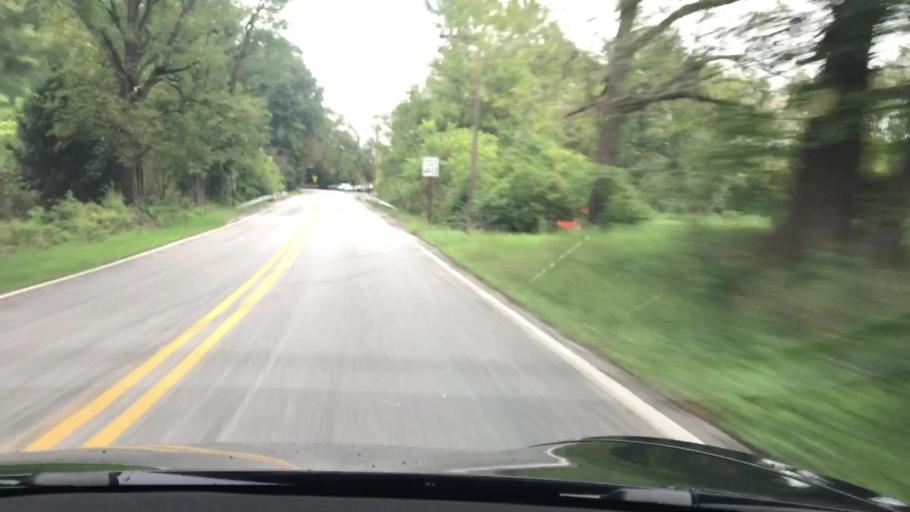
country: US
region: Pennsylvania
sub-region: York County
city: Weigelstown
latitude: 39.9451
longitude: -76.8611
